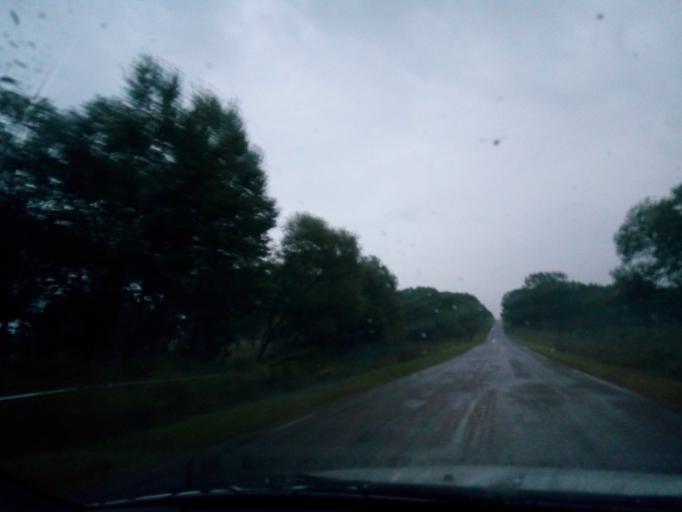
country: RU
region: Primorskiy
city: Lazo
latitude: 45.8701
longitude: 133.6993
